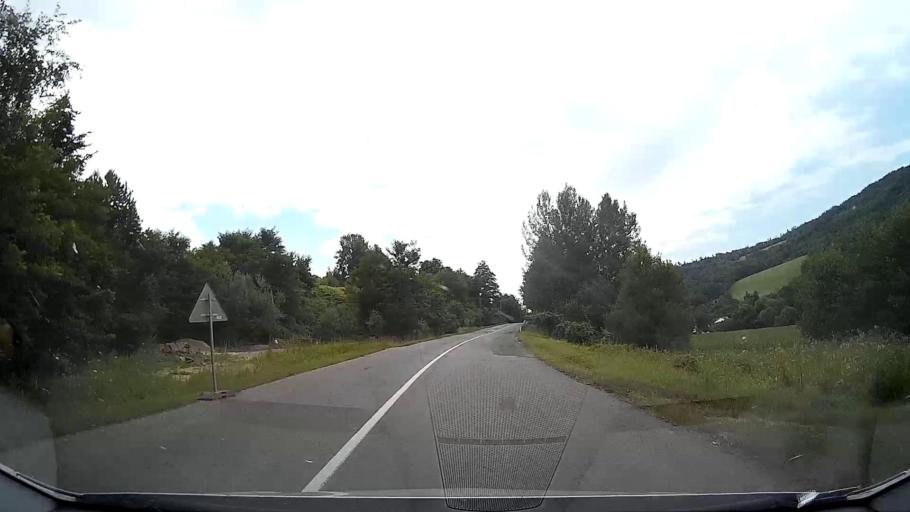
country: SK
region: Banskobystricky
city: Tisovec
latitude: 48.6288
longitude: 19.9524
